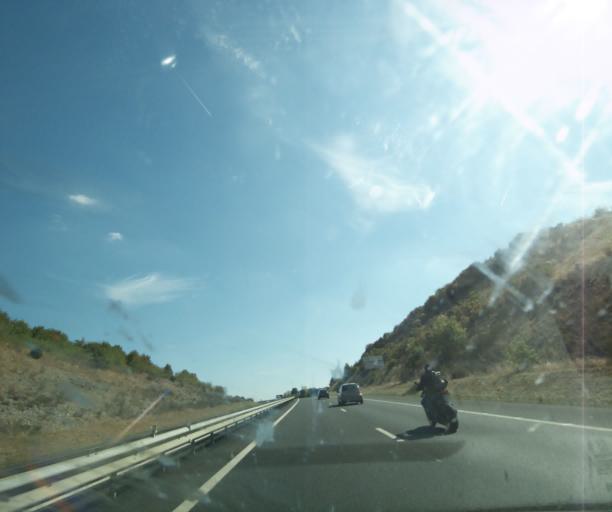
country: FR
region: Limousin
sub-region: Departement de la Correze
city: Brive-la-Gaillarde
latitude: 45.0565
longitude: 1.5082
